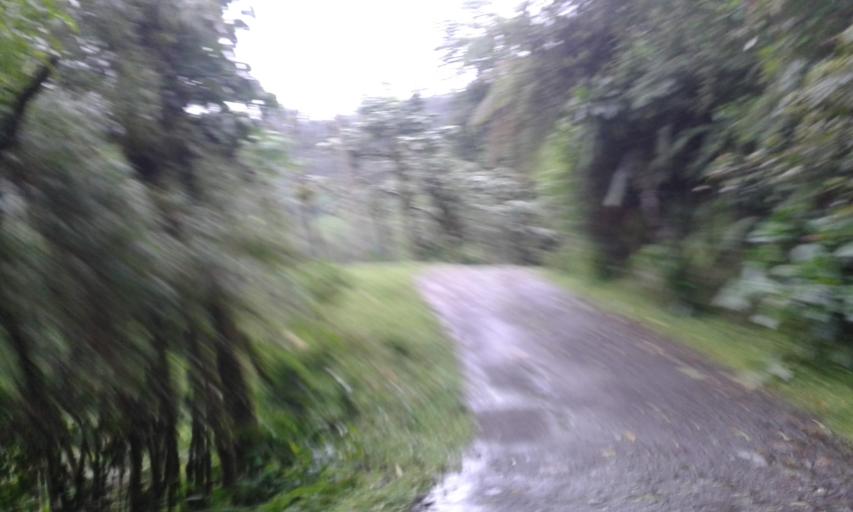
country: CR
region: San Jose
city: Ipis
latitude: 10.0317
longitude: -83.9339
